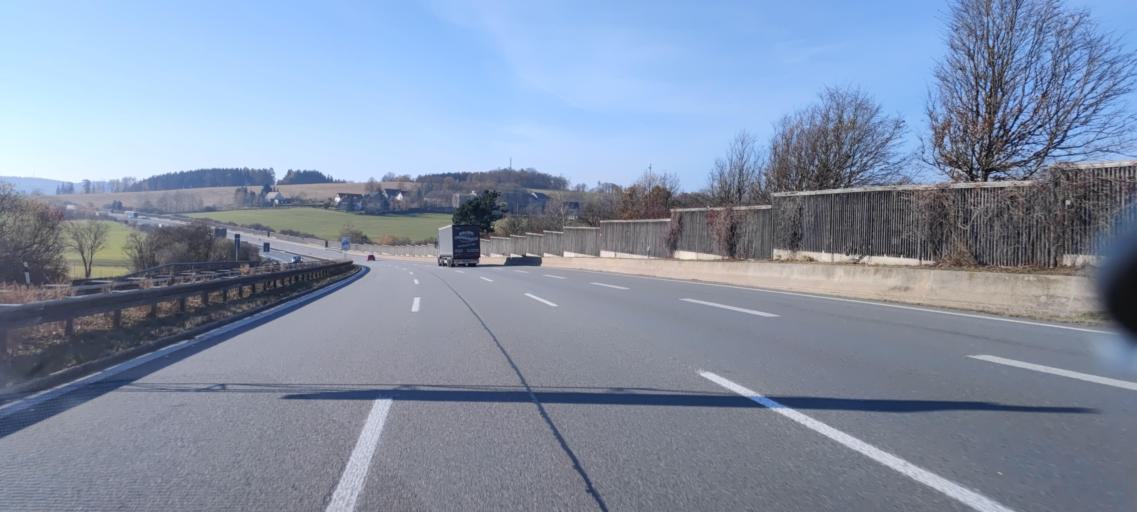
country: DE
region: Saxony
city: Weischlitz
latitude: 50.4344
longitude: 12.0882
